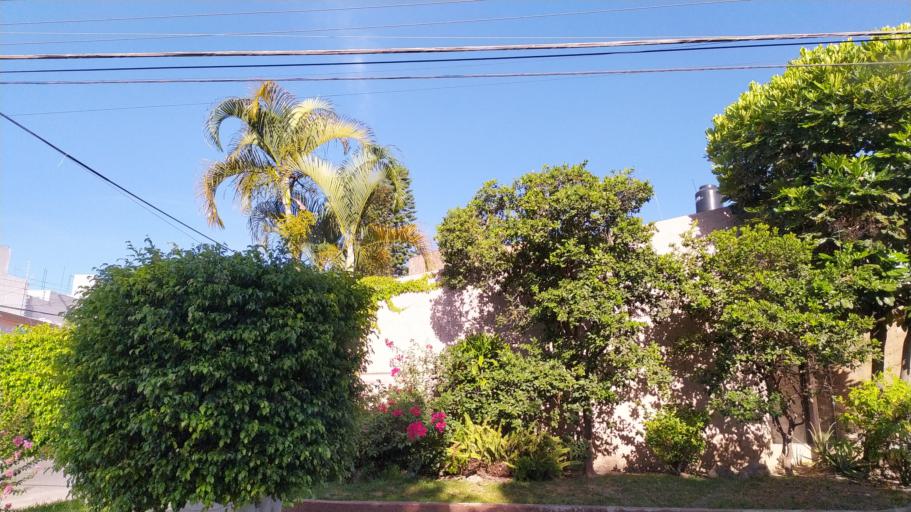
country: MX
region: Jalisco
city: Guadalajara
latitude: 20.6635
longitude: -103.4267
